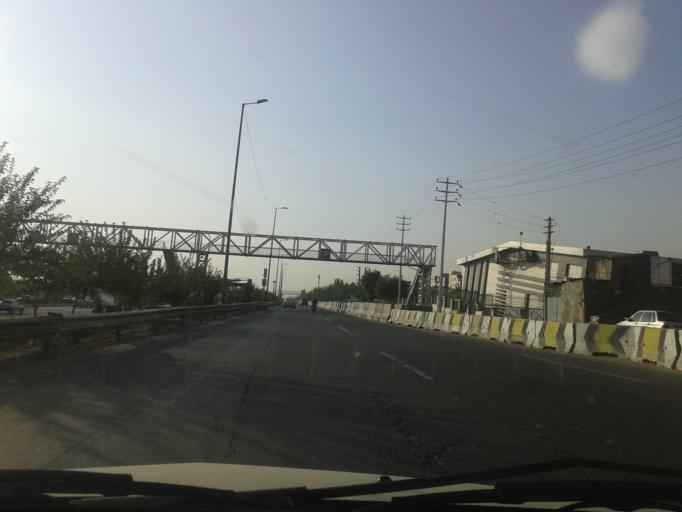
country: IR
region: Tehran
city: Eslamshahr
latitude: 35.6534
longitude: 51.2667
